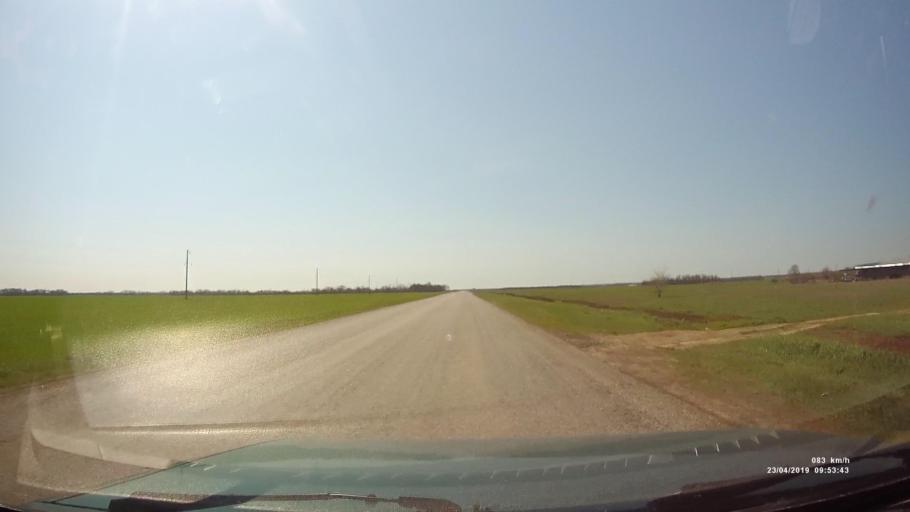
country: RU
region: Rostov
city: Orlovskiy
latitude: 46.8297
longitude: 42.0515
